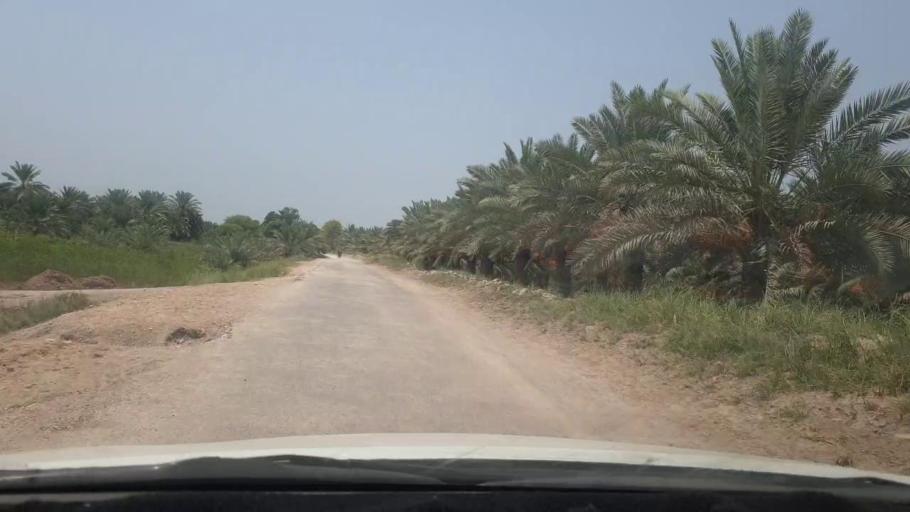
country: PK
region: Sindh
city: Khairpur
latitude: 27.5027
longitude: 68.8674
